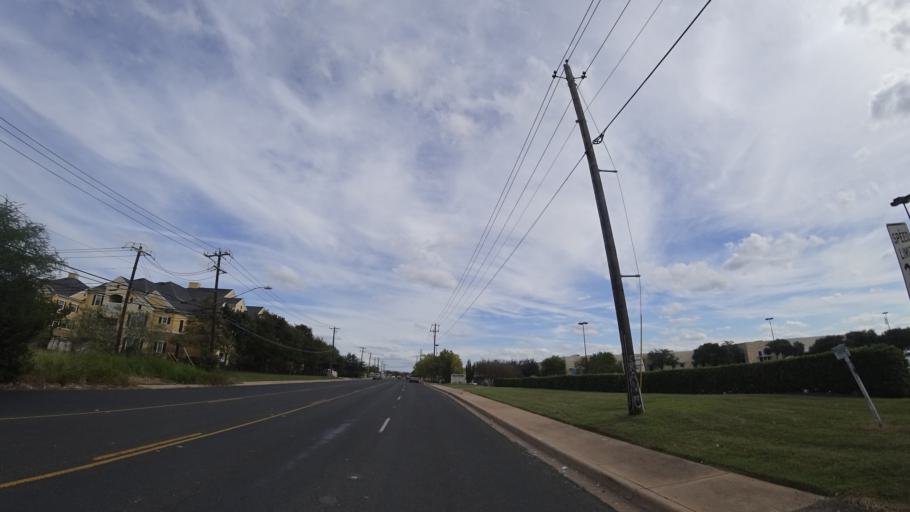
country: US
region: Texas
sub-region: Travis County
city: Austin
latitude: 30.2049
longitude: -97.7570
